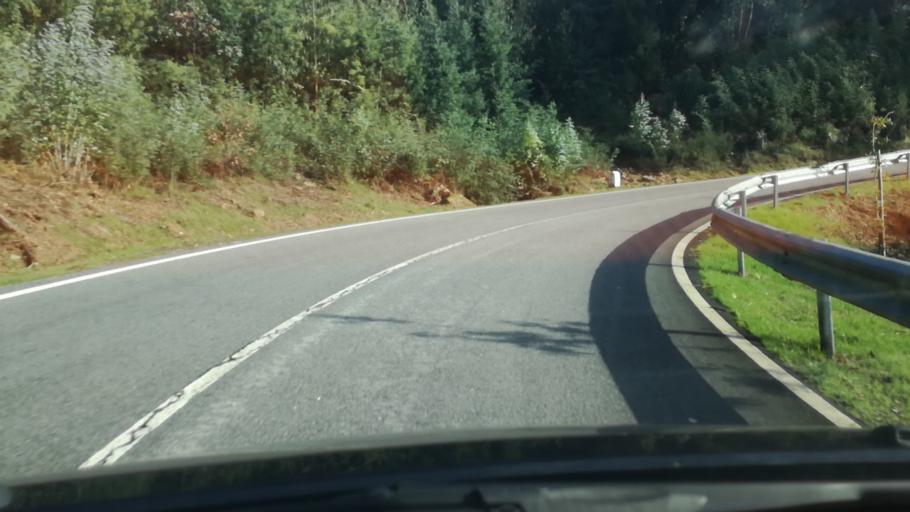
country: PT
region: Braga
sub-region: Povoa de Lanhoso
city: Povoa de Lanhoso
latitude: 41.5308
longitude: -8.3191
